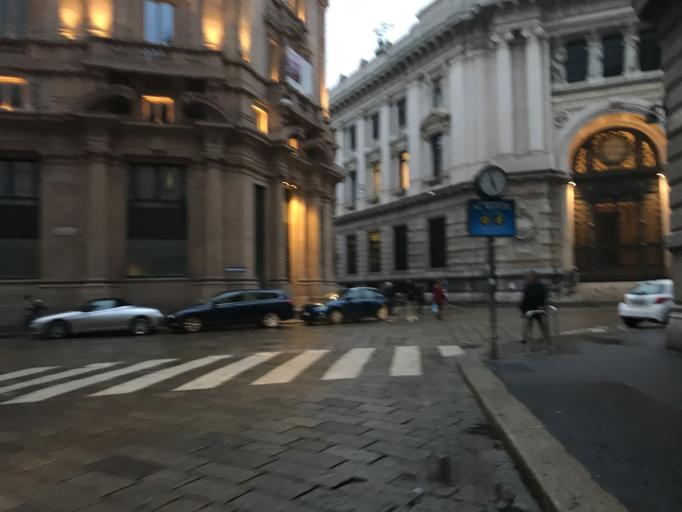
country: IT
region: Lombardy
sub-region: Citta metropolitana di Milano
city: Milano
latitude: 45.4650
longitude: 9.1853
